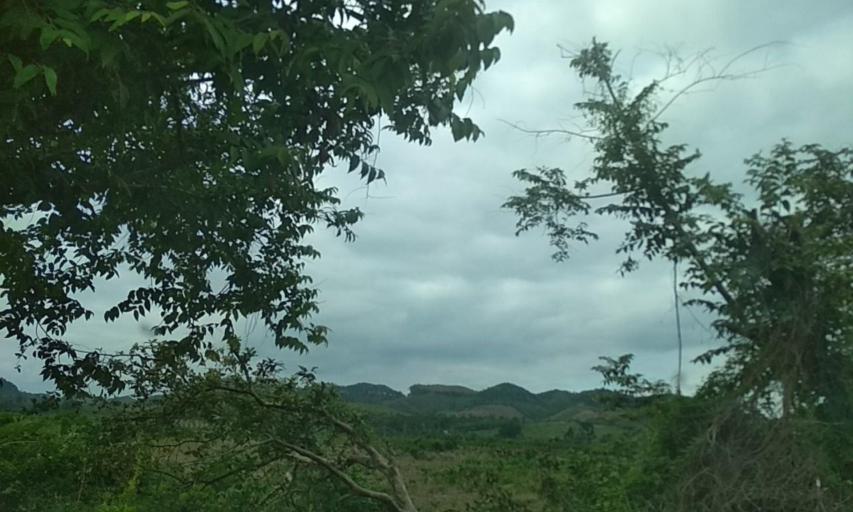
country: MX
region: Veracruz
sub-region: Papantla
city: Polutla
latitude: 20.5759
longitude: -97.2505
